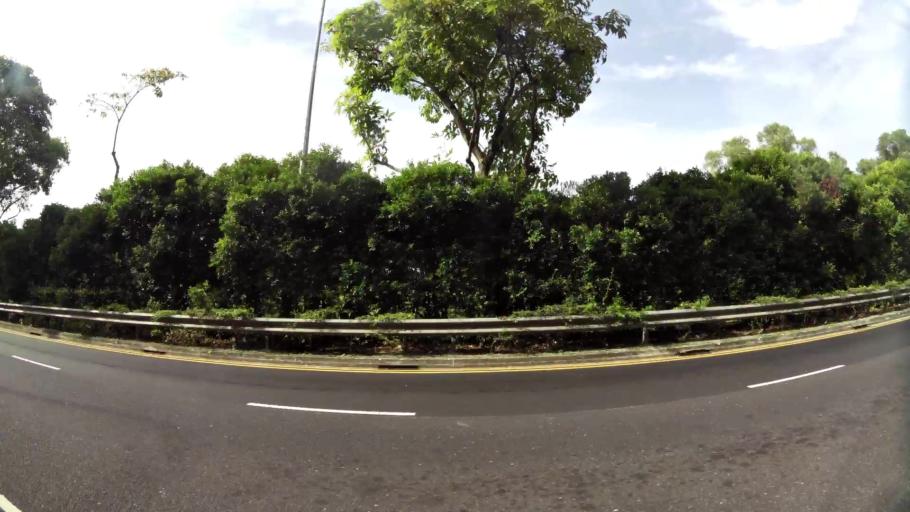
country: MY
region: Johor
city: Johor Bahru
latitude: 1.3464
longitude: 103.6384
